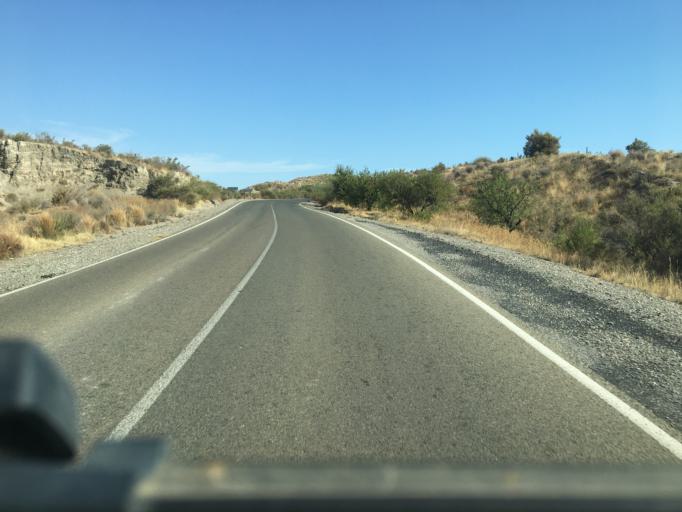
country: ES
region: Andalusia
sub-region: Provincia de Almeria
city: Huercal-Overa
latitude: 37.4232
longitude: -1.9700
